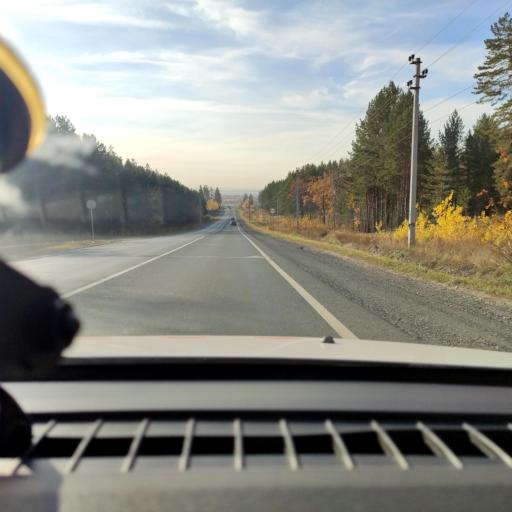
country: RU
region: Samara
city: Volzhskiy
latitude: 53.4441
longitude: 50.1231
